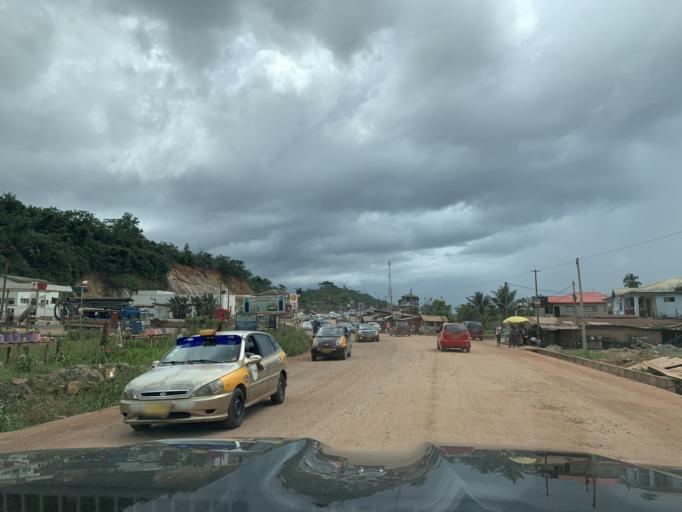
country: GH
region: Western
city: Tarkwa
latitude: 5.3311
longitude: -1.9796
